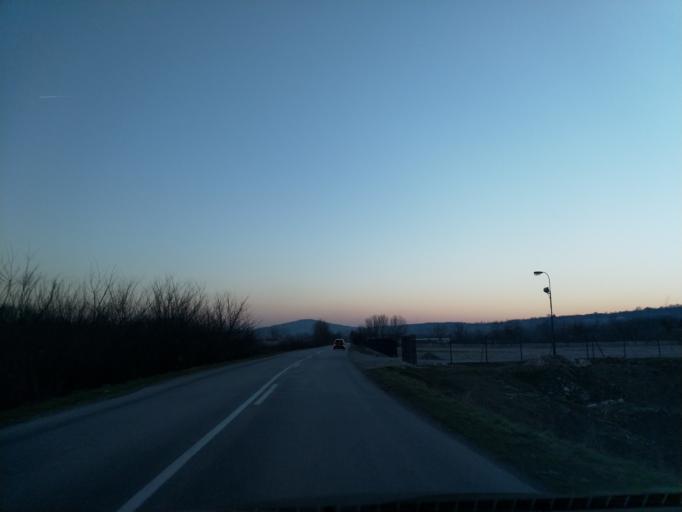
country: RS
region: Central Serbia
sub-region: Pomoravski Okrug
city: Paracin
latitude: 43.8936
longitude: 21.4861
